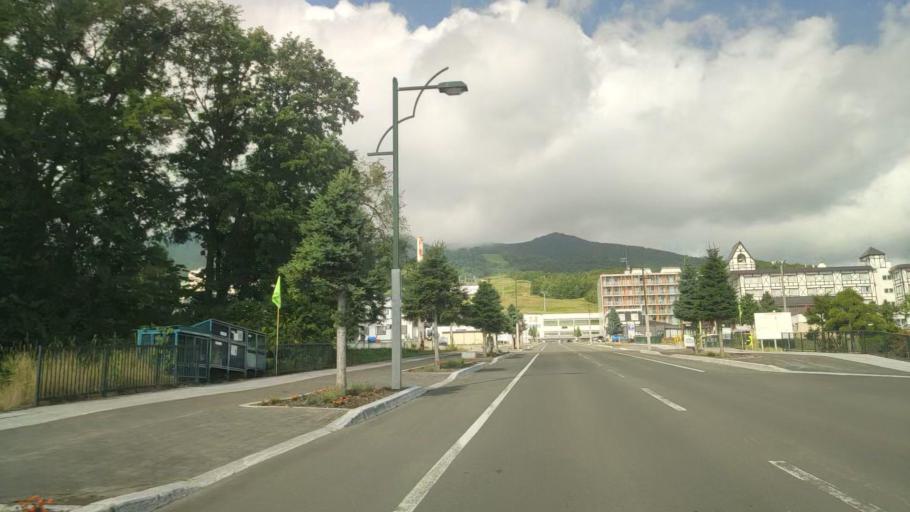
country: JP
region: Hokkaido
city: Shimo-furano
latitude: 43.3434
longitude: 142.3637
